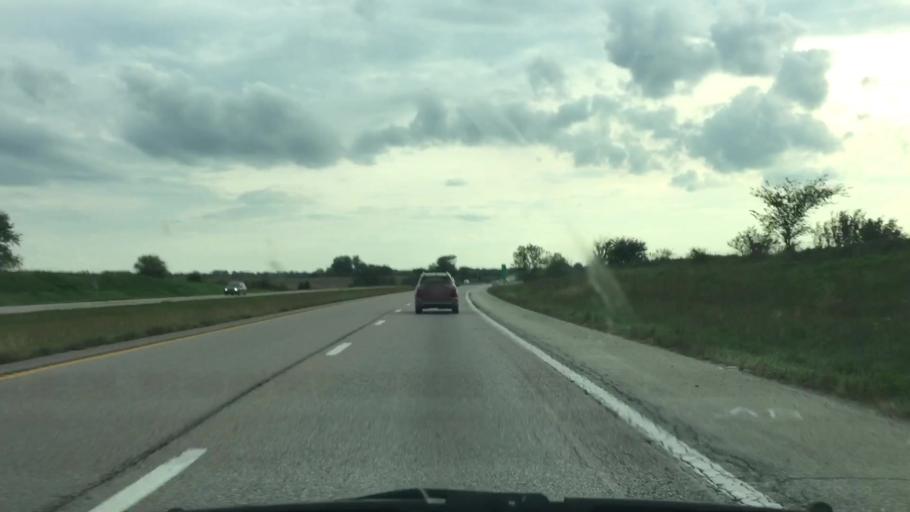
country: US
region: Missouri
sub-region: Clinton County
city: Lathrop
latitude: 39.5220
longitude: -94.2821
